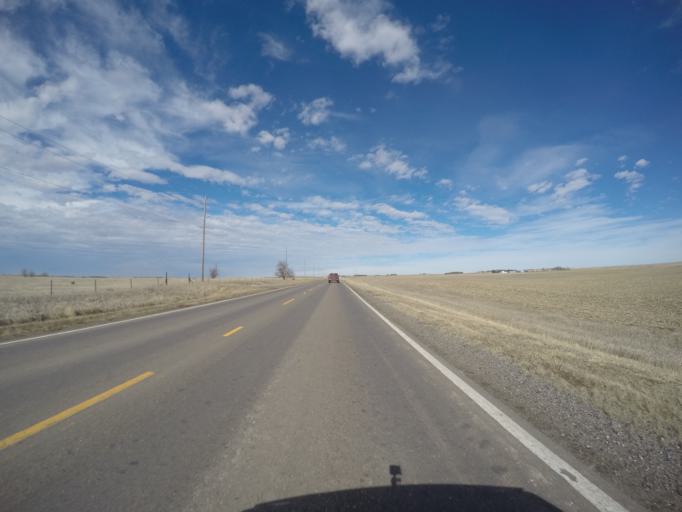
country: US
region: Nebraska
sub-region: Kearney County
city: Minden
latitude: 40.3275
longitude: -98.9530
